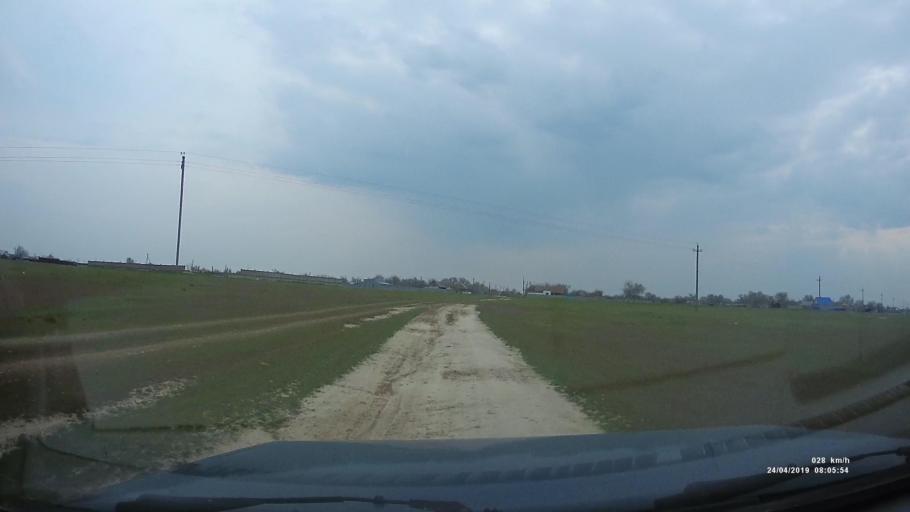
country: RU
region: Kalmykiya
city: Priyutnoye
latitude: 46.1002
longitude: 43.4883
